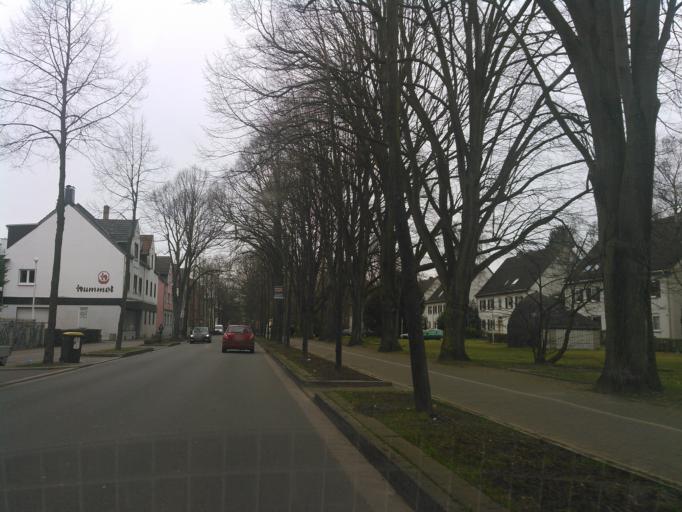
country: DE
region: North Rhine-Westphalia
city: Marl
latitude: 51.6699
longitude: 7.1134
